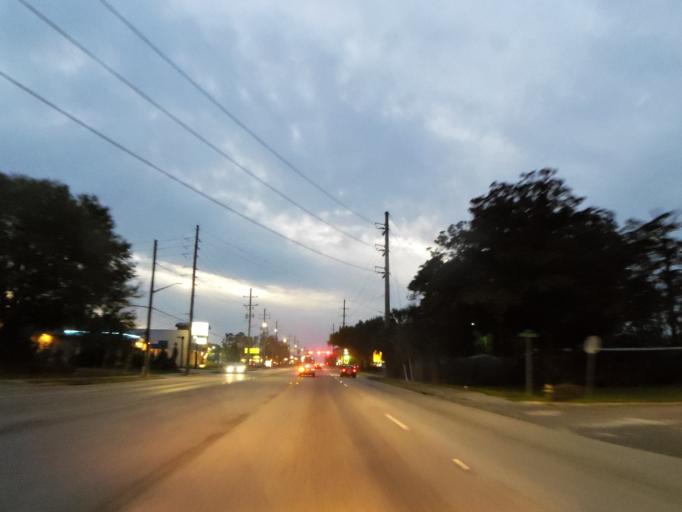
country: US
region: Florida
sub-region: Duval County
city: Jacksonville
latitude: 30.3522
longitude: -81.5669
